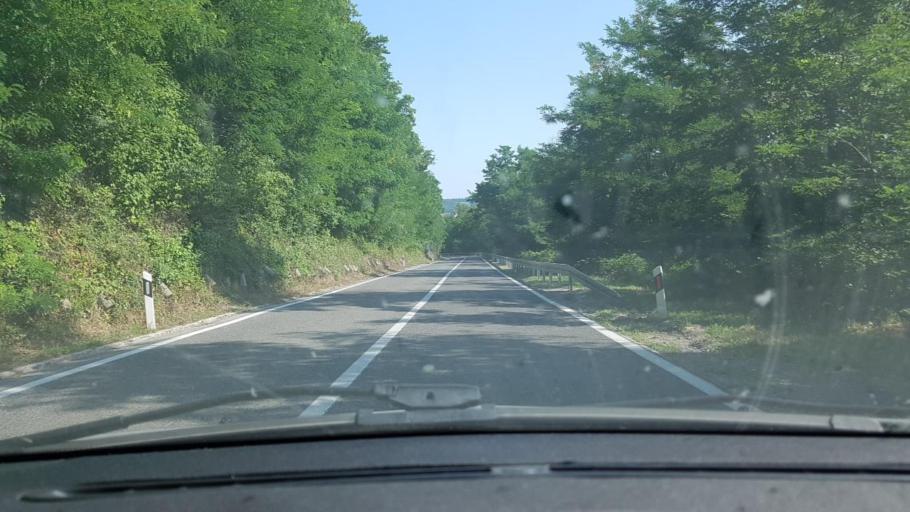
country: BA
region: Federation of Bosnia and Herzegovina
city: Pecigrad
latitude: 45.0585
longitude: 15.8924
